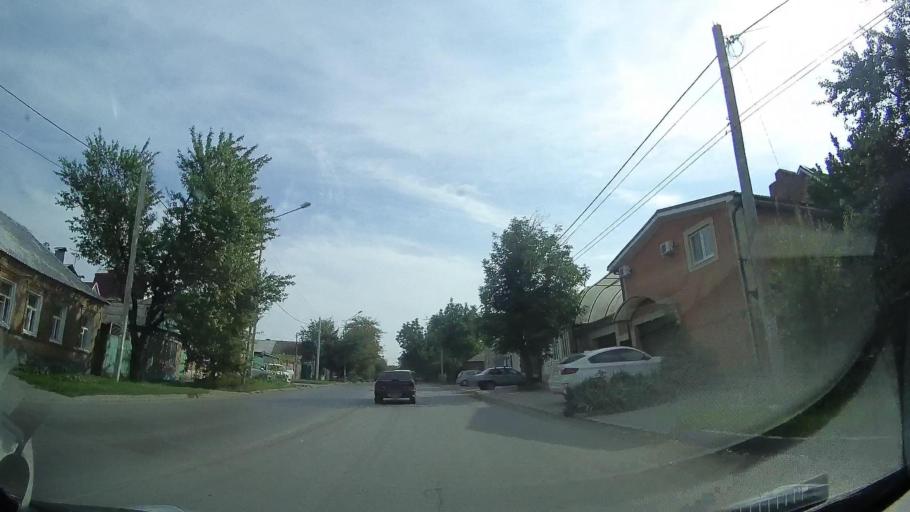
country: RU
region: Rostov
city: Severnyy
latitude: 47.2695
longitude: 39.7064
